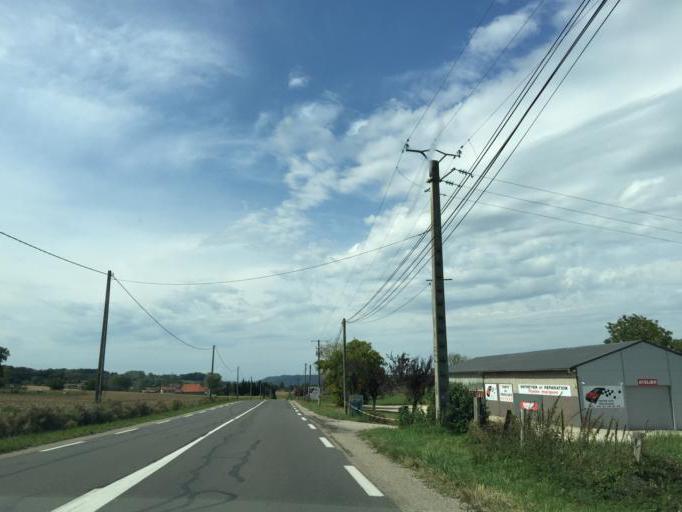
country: FR
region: Rhone-Alpes
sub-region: Departement de l'Isere
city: Saint-Didier-de-la-Tour
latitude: 45.5504
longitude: 5.5028
